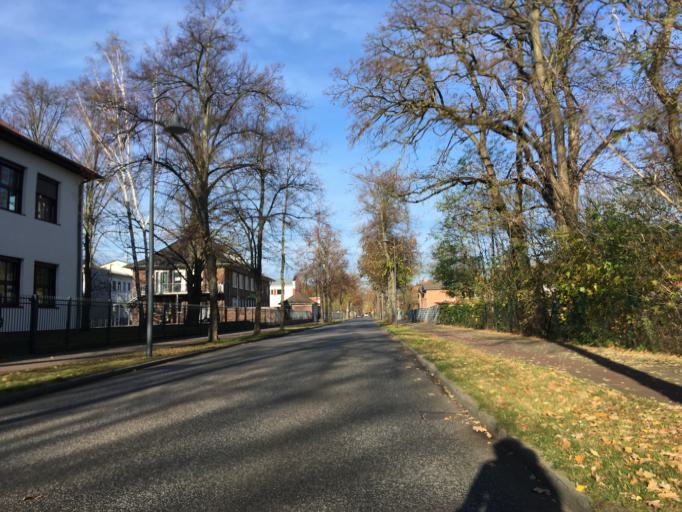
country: DE
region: Brandenburg
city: Wildau
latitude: 52.3291
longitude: 13.6388
